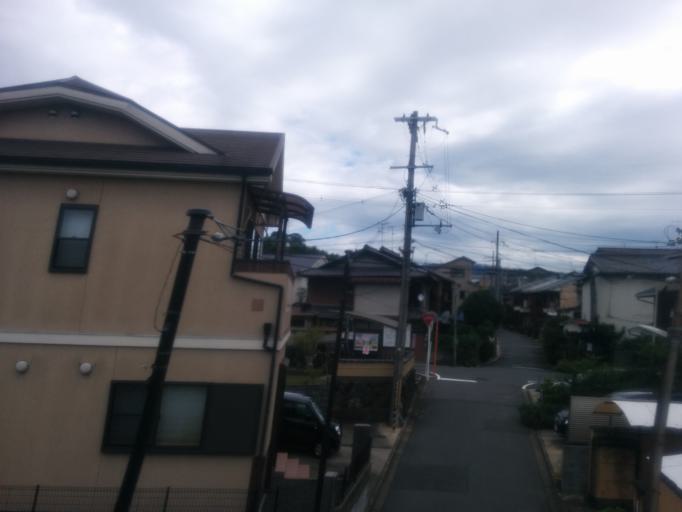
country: JP
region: Kyoto
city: Kyoto
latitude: 34.9575
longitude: 135.7772
